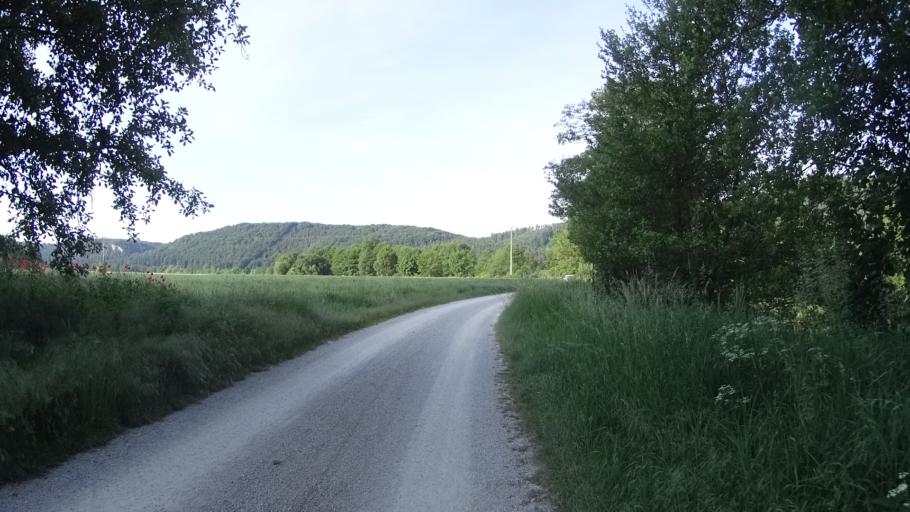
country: DE
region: Bavaria
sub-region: Lower Bavaria
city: Riedenburg
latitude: 48.9914
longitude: 11.6330
